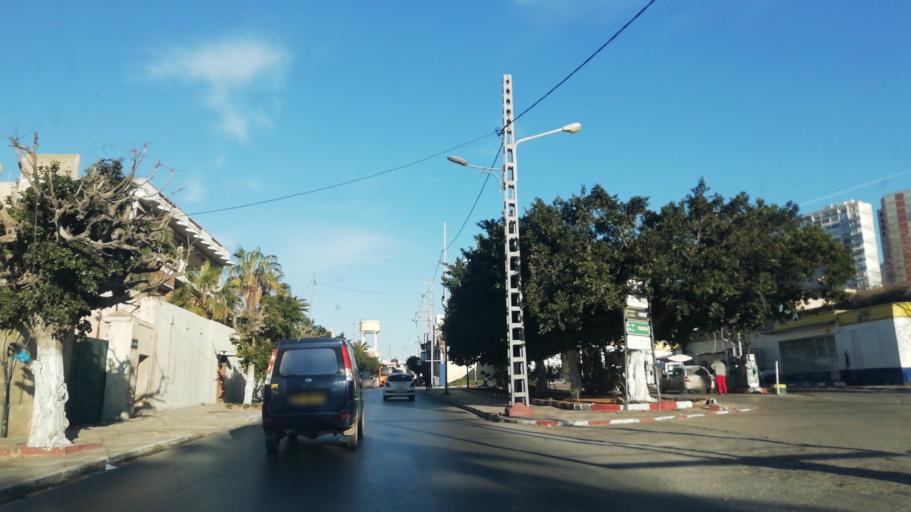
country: DZ
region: Oran
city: Oran
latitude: 35.7059
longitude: -0.6273
